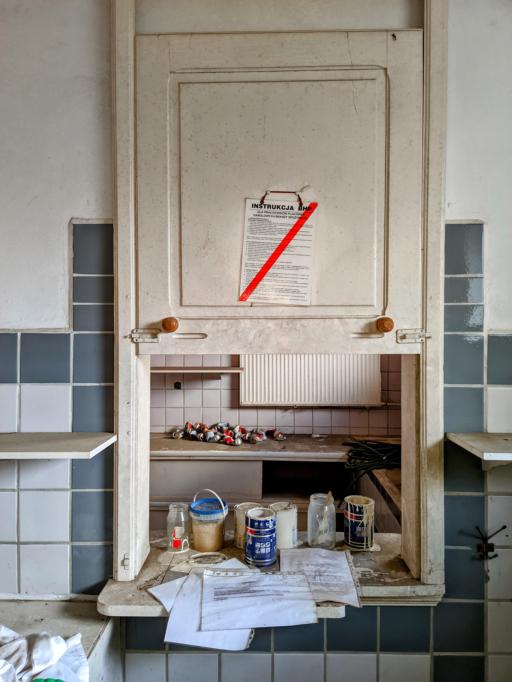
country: PL
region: Lubusz
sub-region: Powiat swiebodzinski
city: Lubrza
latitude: 52.3119
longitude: 15.4256
